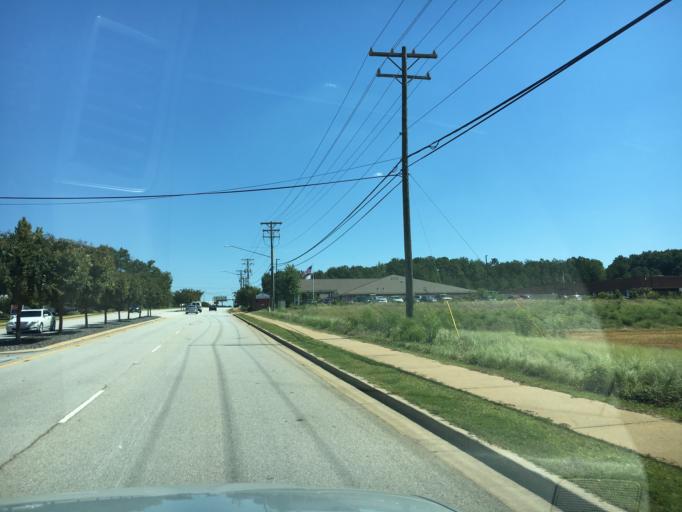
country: US
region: South Carolina
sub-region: Greenville County
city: Greenville
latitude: 34.8344
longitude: -82.3390
